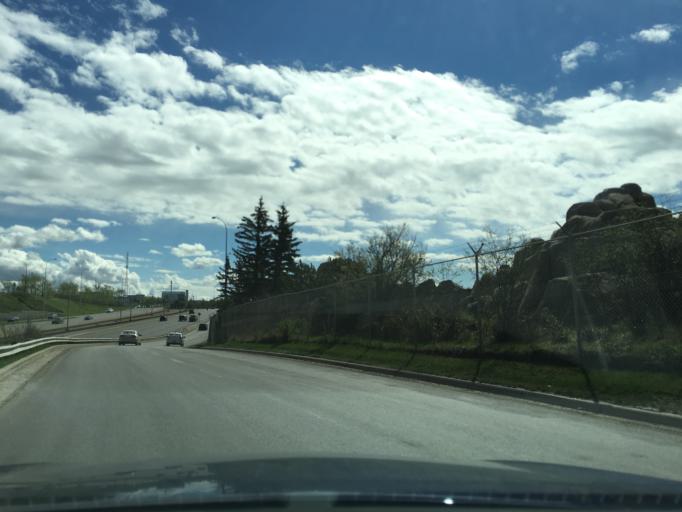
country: CA
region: Alberta
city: Calgary
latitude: 51.0475
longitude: -114.0318
